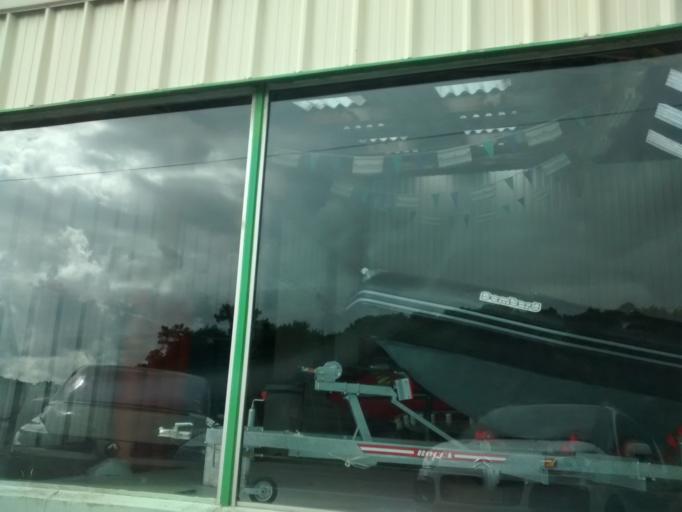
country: FR
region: Brittany
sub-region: Departement des Cotes-d'Armor
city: Minihy-Treguier
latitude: 48.7837
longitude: -3.2157
